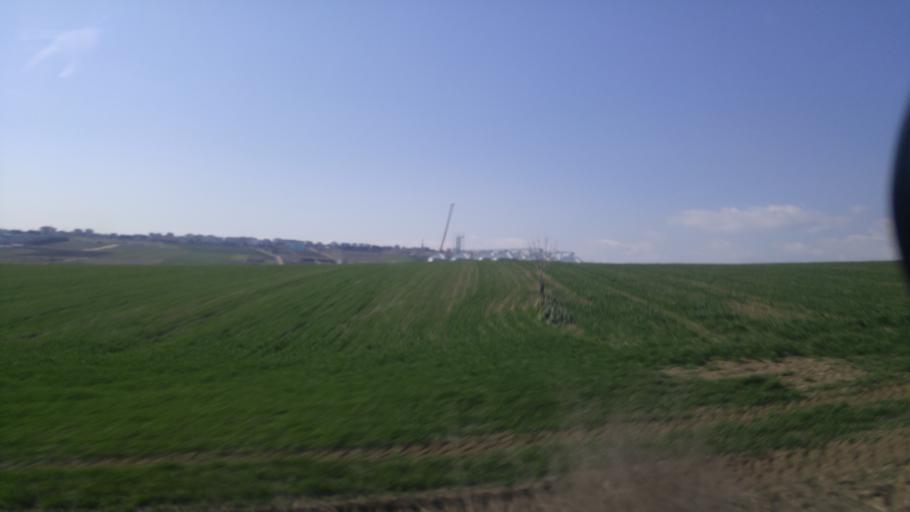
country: TR
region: Istanbul
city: Canta
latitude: 41.0809
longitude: 28.1072
